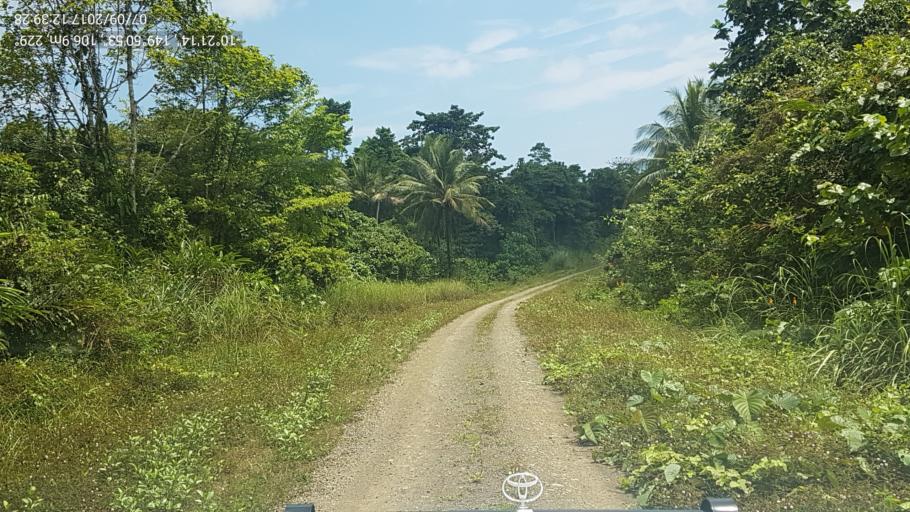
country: PG
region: Milne Bay
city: Alotau
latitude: -10.3542
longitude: 149.8483
